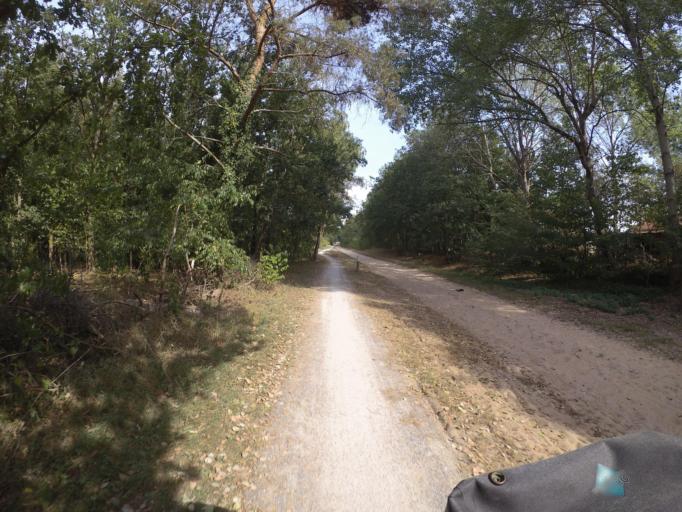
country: NL
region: Drenthe
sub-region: Gemeente Westerveld
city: Havelte
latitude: 52.7988
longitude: 6.2522
